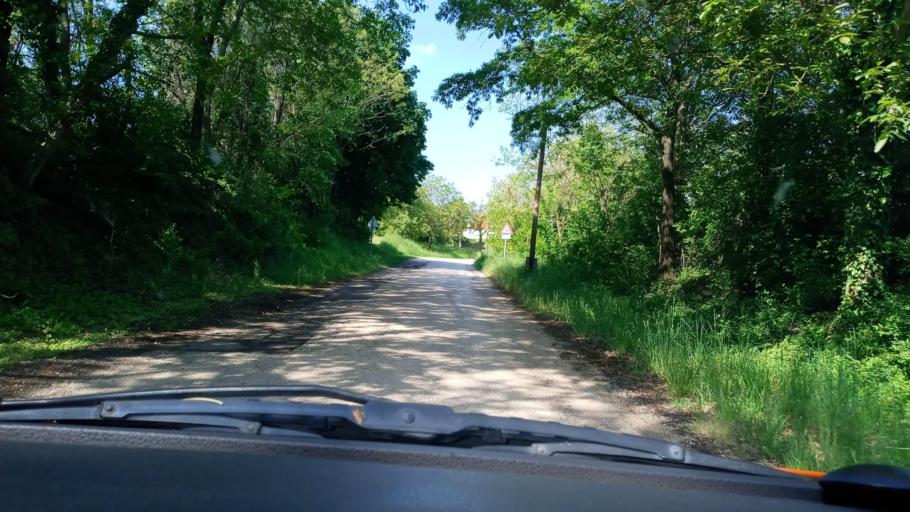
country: HU
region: Baranya
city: Harkany
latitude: 45.9046
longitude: 18.2530
